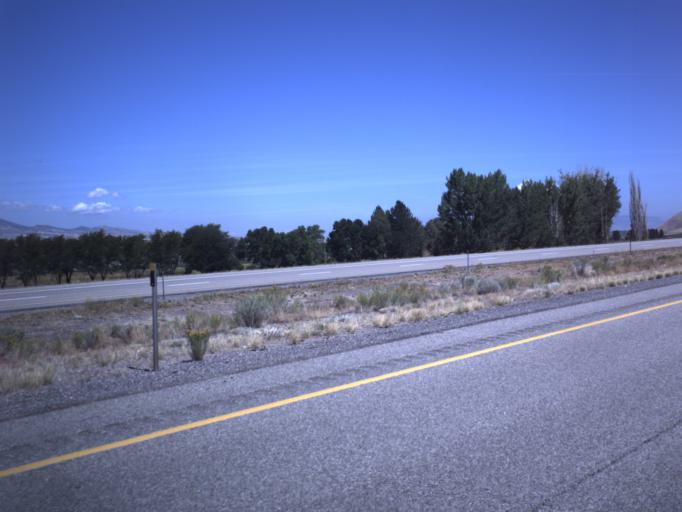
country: US
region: Utah
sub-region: Sevier County
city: Aurora
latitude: 38.9043
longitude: -111.9016
